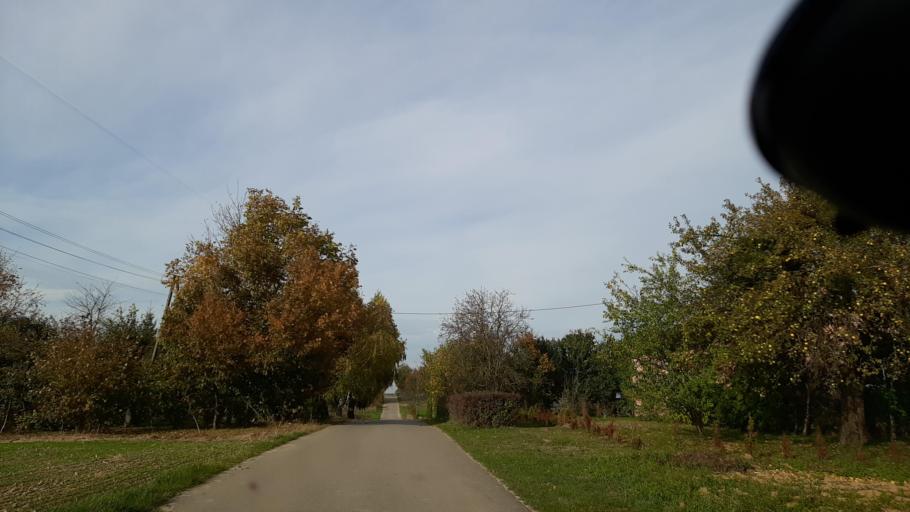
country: PL
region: Lublin Voivodeship
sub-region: Powiat lubelski
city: Jastkow
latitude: 51.3330
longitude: 22.4111
